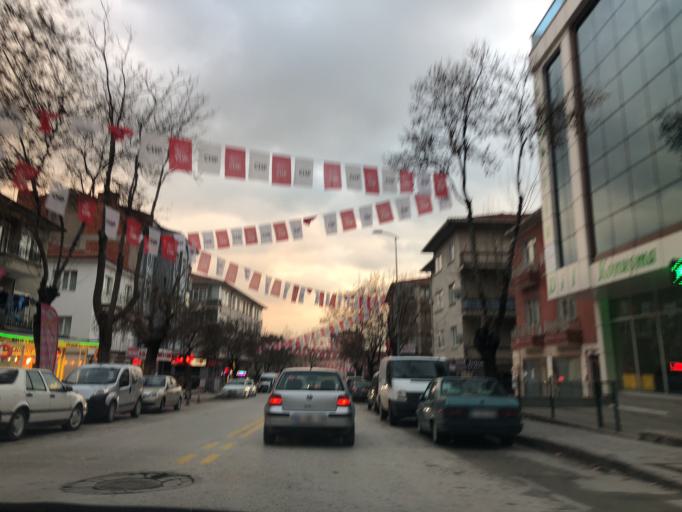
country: TR
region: Ankara
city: Ankara
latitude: 39.9648
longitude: 32.8087
